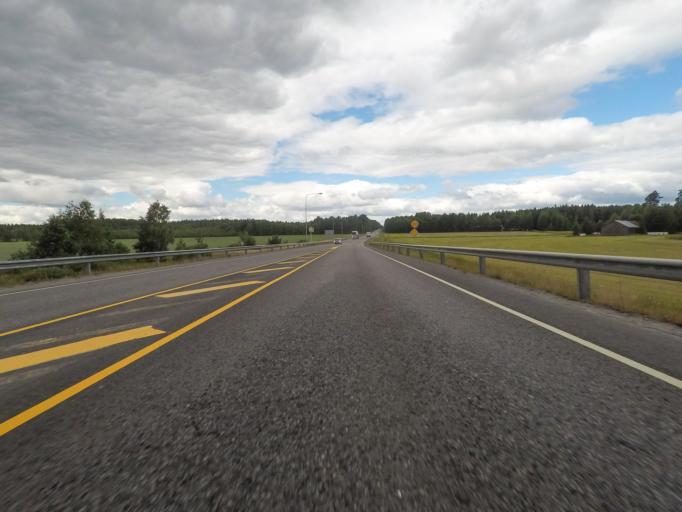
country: FI
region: Varsinais-Suomi
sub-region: Turku
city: Piikkioe
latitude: 60.4443
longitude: 22.4849
